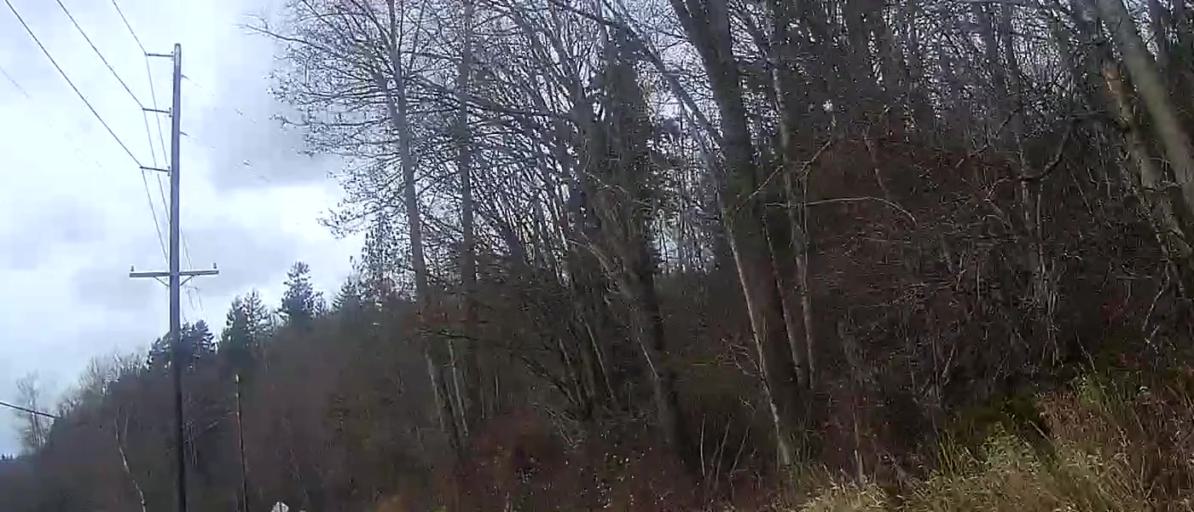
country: US
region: Washington
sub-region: Skagit County
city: Burlington
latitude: 48.5603
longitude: -122.3213
